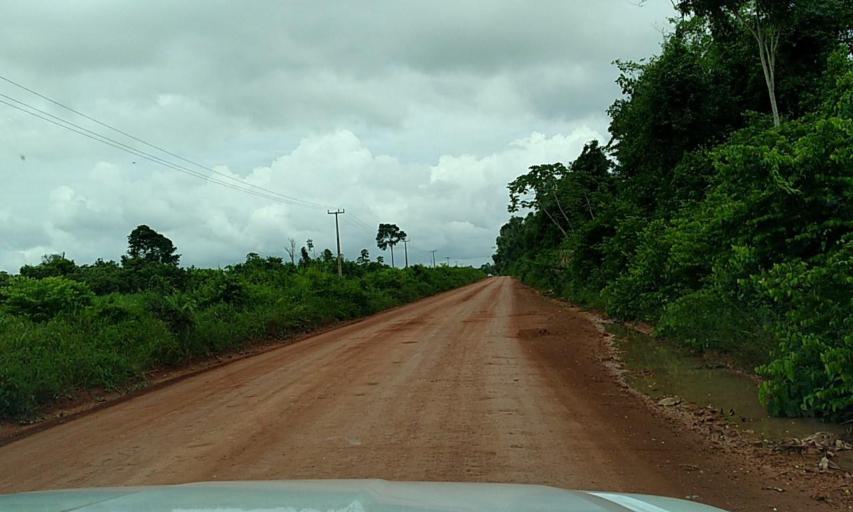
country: BR
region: Para
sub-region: Senador Jose Porfirio
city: Senador Jose Porfirio
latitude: -2.6674
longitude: -51.8392
